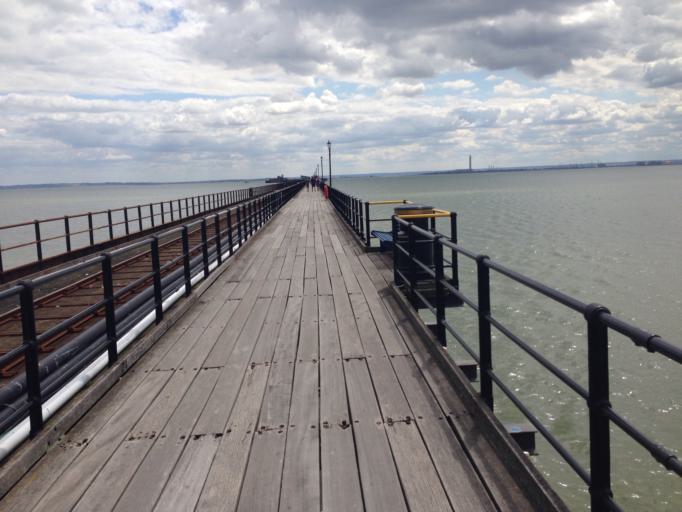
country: GB
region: England
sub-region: Southend-on-Sea
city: Southend-on-Sea
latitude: 51.5280
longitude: 0.7174
